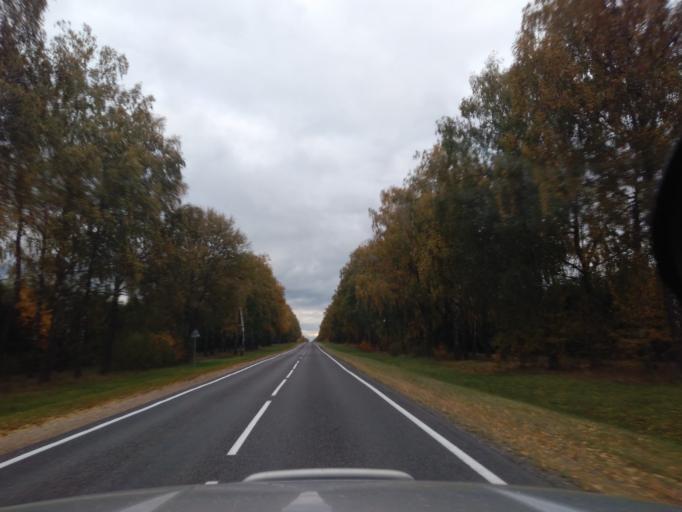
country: BY
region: Minsk
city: Slutsk
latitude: 53.2216
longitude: 27.4997
